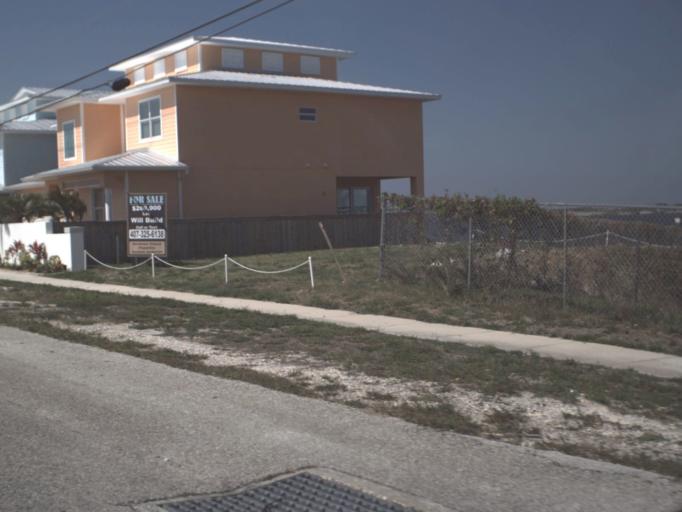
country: US
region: Florida
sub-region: Brevard County
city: South Patrick Shores
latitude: 28.1926
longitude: -80.6574
